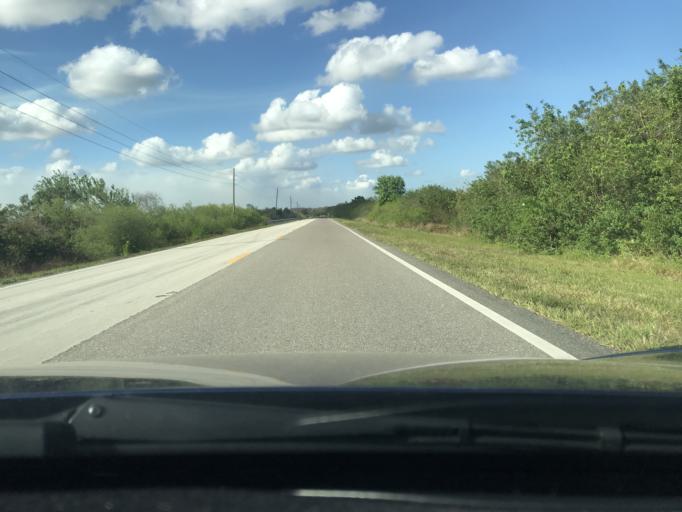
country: US
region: Florida
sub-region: Okeechobee County
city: Taylor Creek
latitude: 27.2806
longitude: -80.6959
